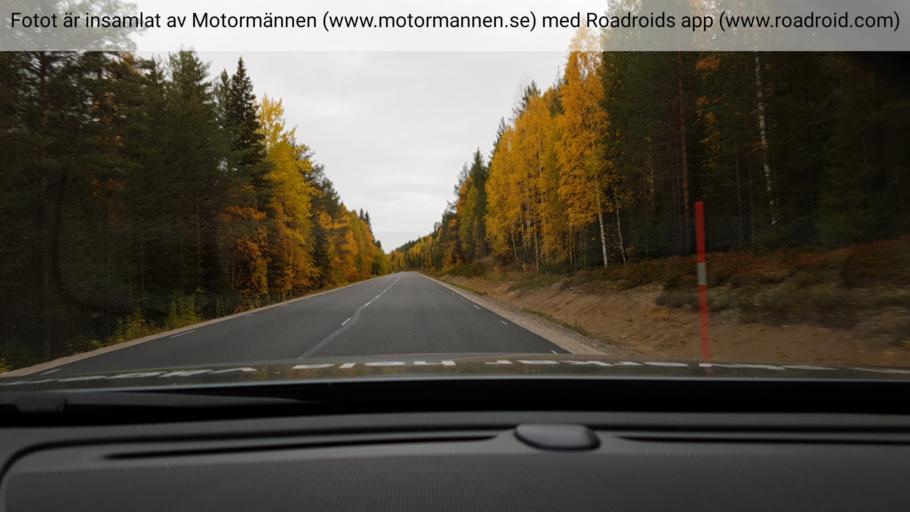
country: SE
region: Norrbotten
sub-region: Overkalix Kommun
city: OEverkalix
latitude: 66.4708
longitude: 22.7917
